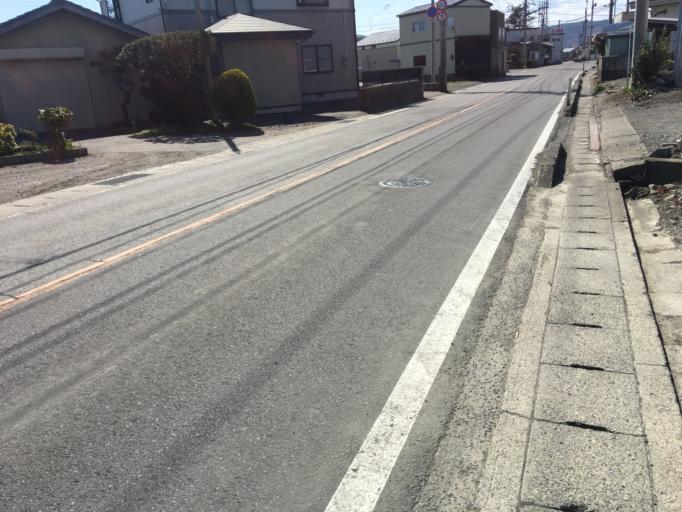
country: JP
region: Aomori
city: Hachinohe
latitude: 40.2056
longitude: 141.7945
